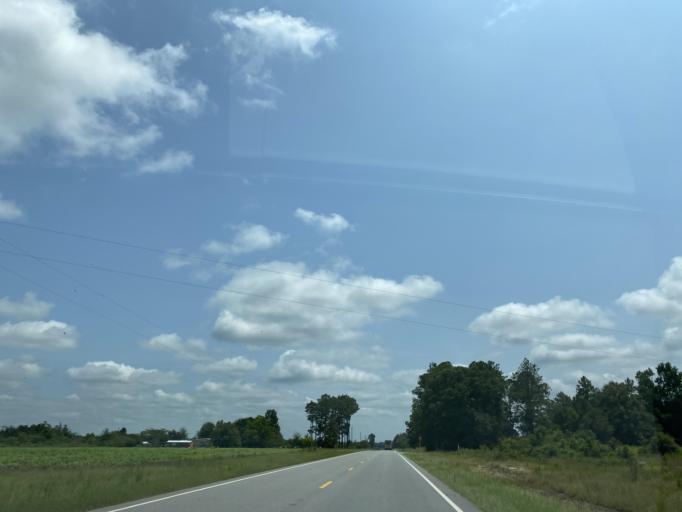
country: US
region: Georgia
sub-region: Jeff Davis County
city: Hazlehurst
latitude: 31.7326
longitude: -82.5338
